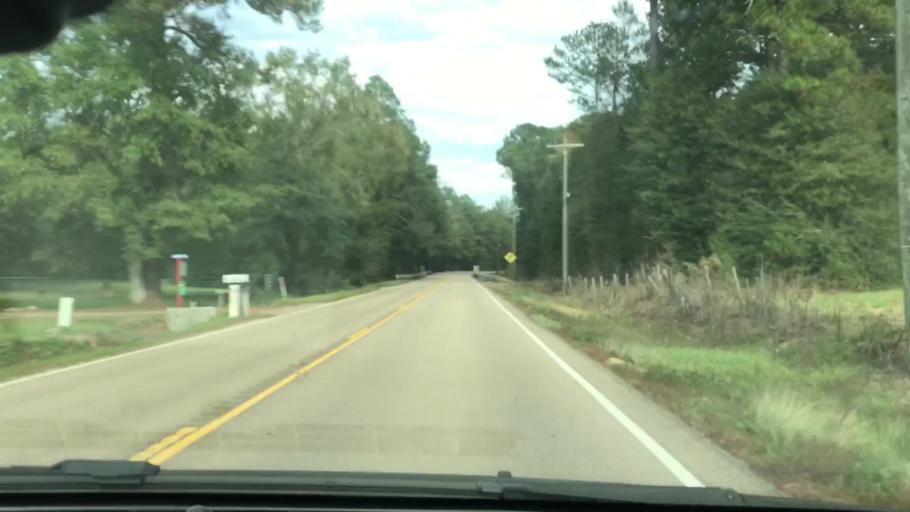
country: US
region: Louisiana
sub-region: Saint Tammany Parish
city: Abita Springs
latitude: 30.5024
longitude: -89.9921
